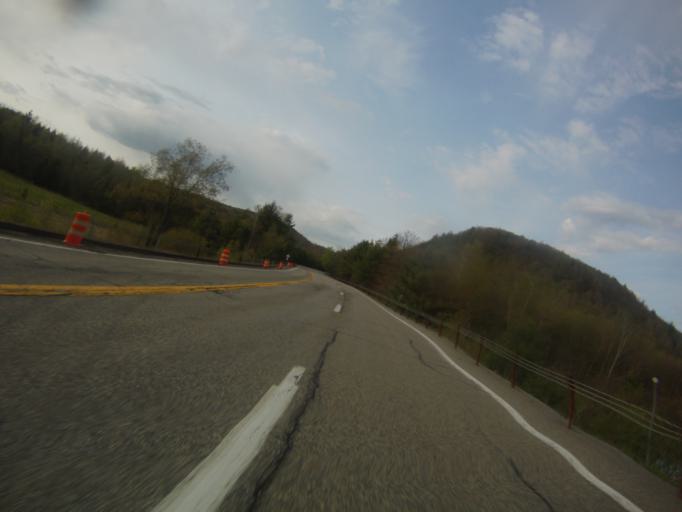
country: US
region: New York
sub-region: Essex County
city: Ticonderoga
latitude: 43.7340
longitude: -73.5990
